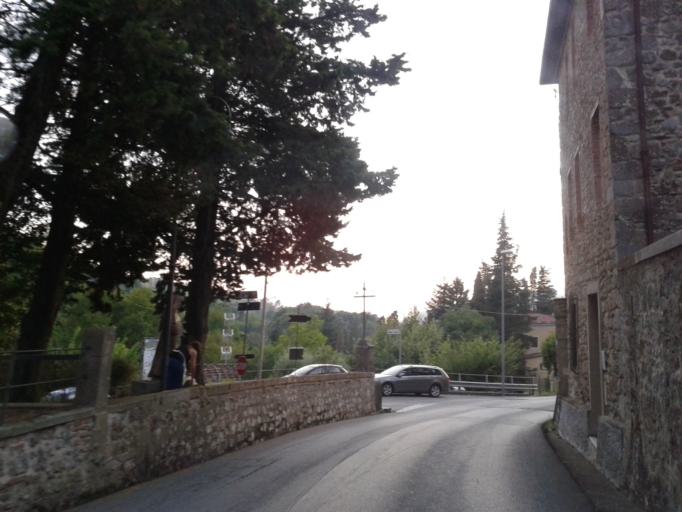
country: IT
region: Tuscany
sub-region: Provincia di Lucca
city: Corsanico-Bargecchia
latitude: 43.9524
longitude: 10.3183
